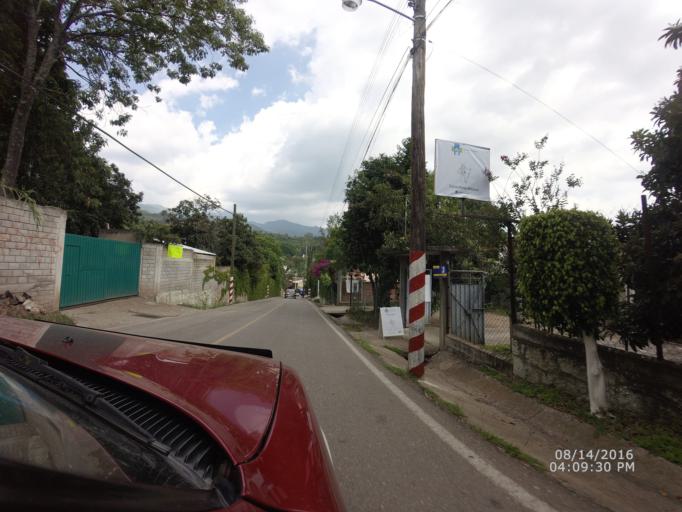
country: MX
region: Oaxaca
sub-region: San Juan Bautista Guelache
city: Fraccionamiento San Miguel
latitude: 17.1856
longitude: -96.7632
